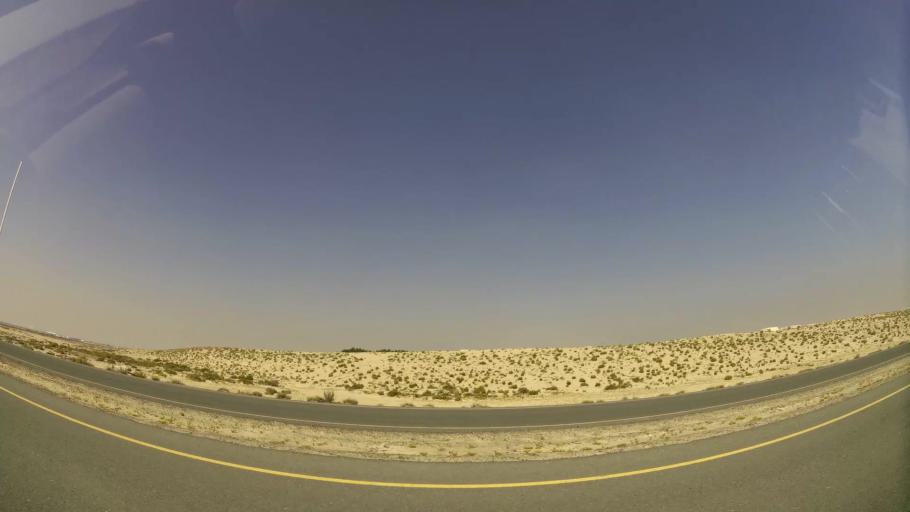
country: AE
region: Dubai
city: Dubai
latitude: 24.9602
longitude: 55.0158
